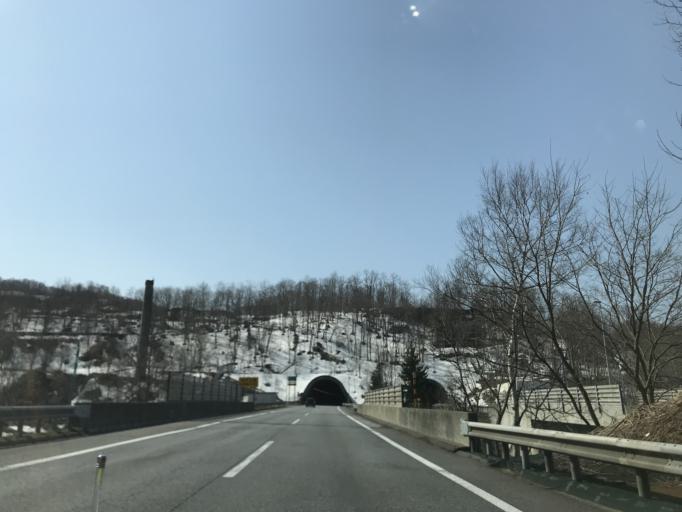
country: JP
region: Hokkaido
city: Bibai
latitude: 43.3091
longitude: 141.8816
